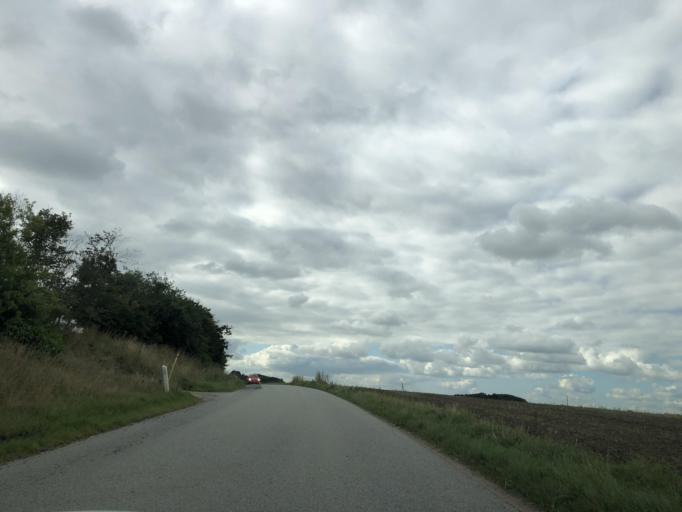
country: DK
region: North Denmark
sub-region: Rebild Kommune
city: Stovring
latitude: 56.9235
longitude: 9.7868
